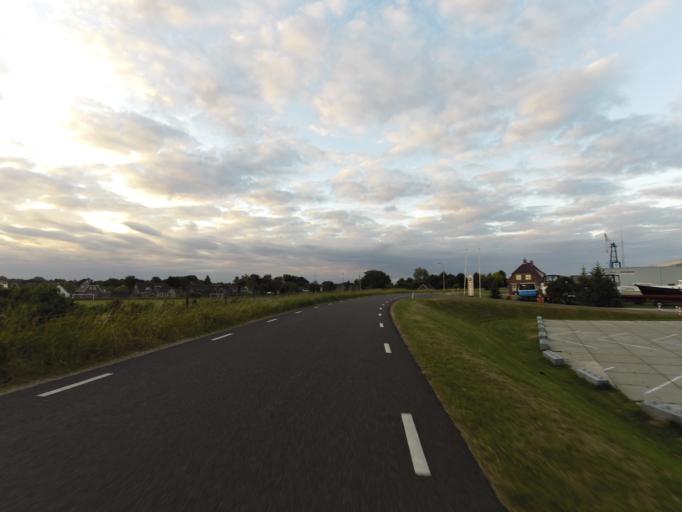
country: NL
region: Gelderland
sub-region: Gemeente Duiven
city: Duiven
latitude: 51.8777
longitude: 5.9906
